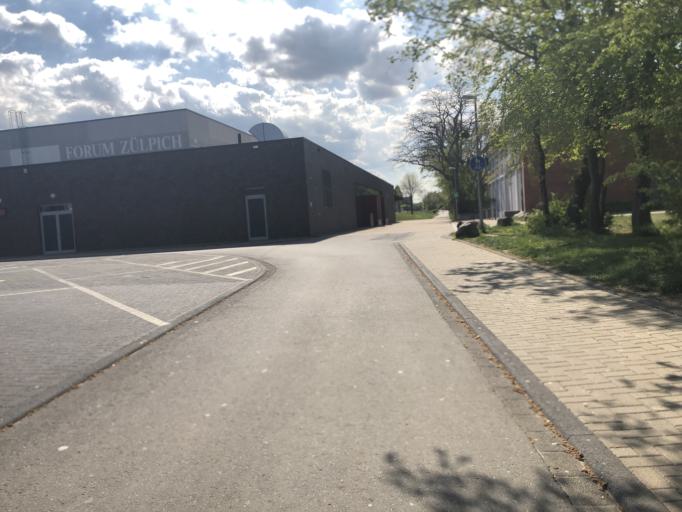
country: DE
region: North Rhine-Westphalia
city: Zulpich
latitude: 50.6912
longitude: 6.6567
